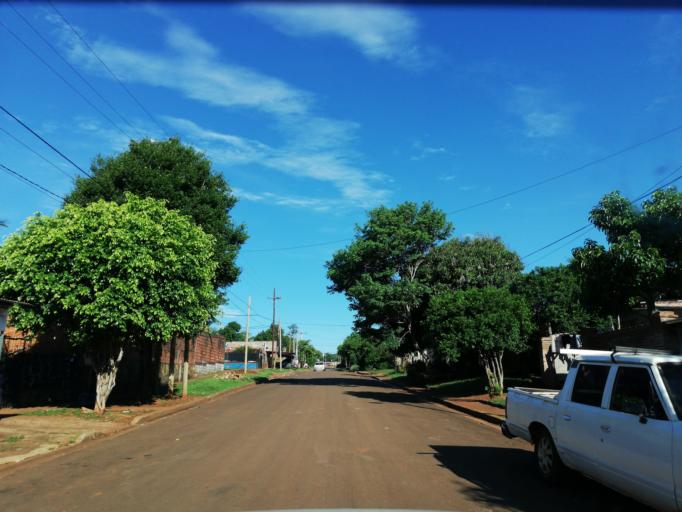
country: AR
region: Misiones
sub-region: Departamento de Capital
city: Posadas
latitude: -27.4059
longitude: -55.9572
